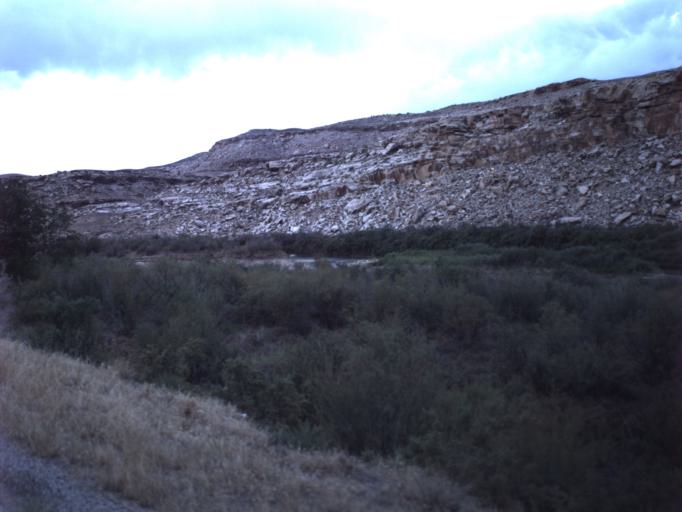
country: US
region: Utah
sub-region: Grand County
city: Moab
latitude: 38.8219
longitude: -109.2835
